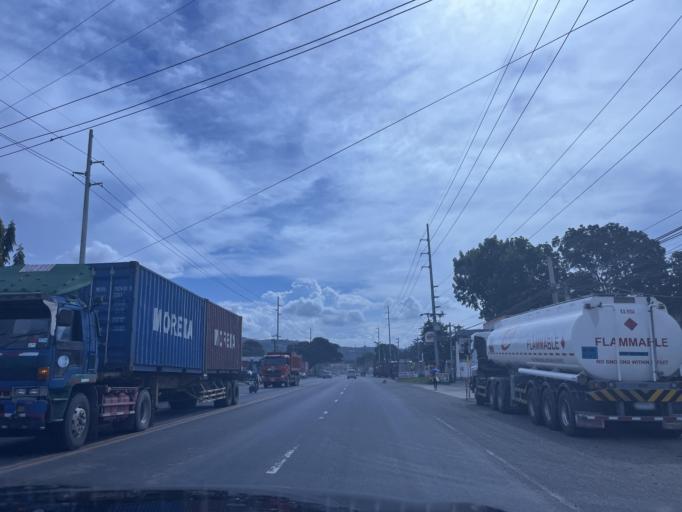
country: PH
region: Northern Mindanao
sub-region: Chartered City of Cagayan de Oro
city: Agusan
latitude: 8.4757
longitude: 124.7166
